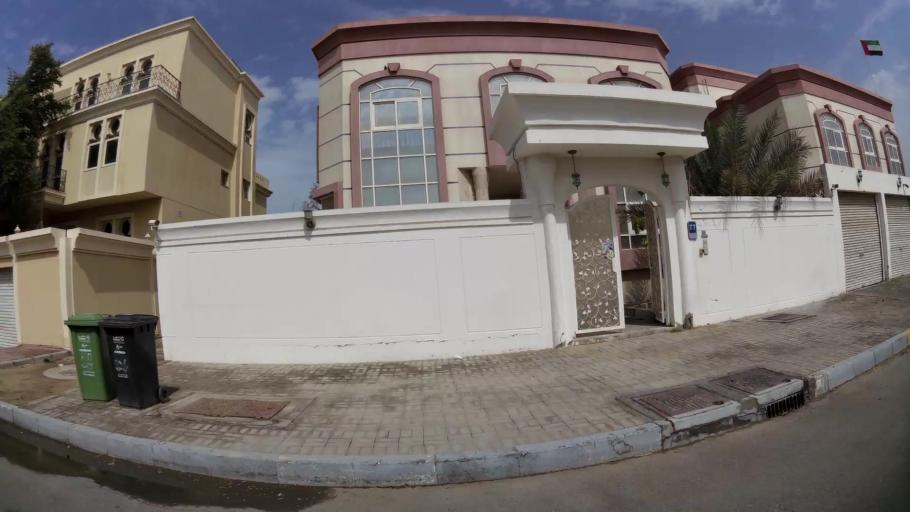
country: AE
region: Abu Dhabi
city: Abu Dhabi
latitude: 24.4155
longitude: 54.4679
